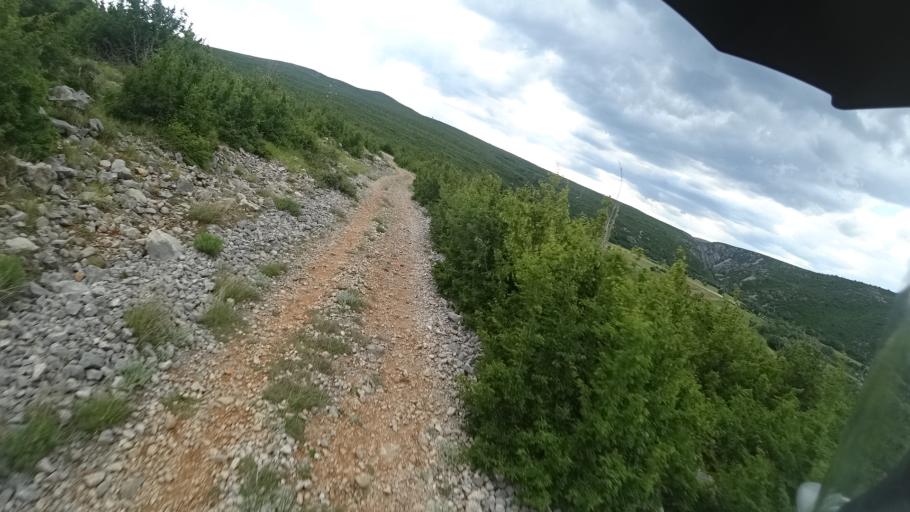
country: HR
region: Zadarska
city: Gracac
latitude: 44.1885
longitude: 15.8896
